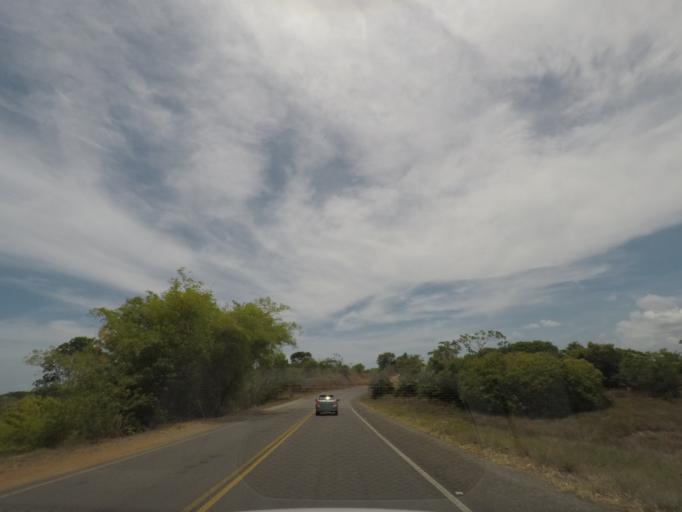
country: BR
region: Bahia
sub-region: Conde
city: Conde
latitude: -12.0456
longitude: -37.7063
